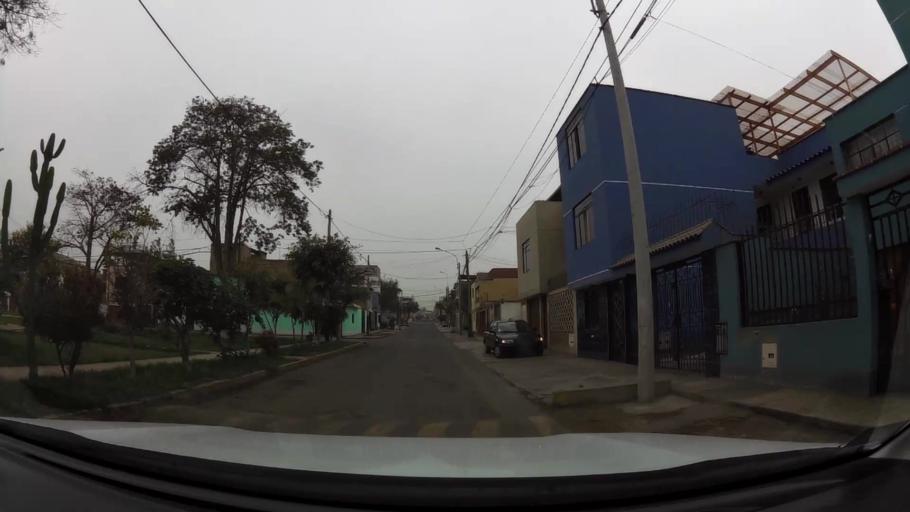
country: PE
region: Lima
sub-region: Lima
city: Surco
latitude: -12.1636
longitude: -76.9772
